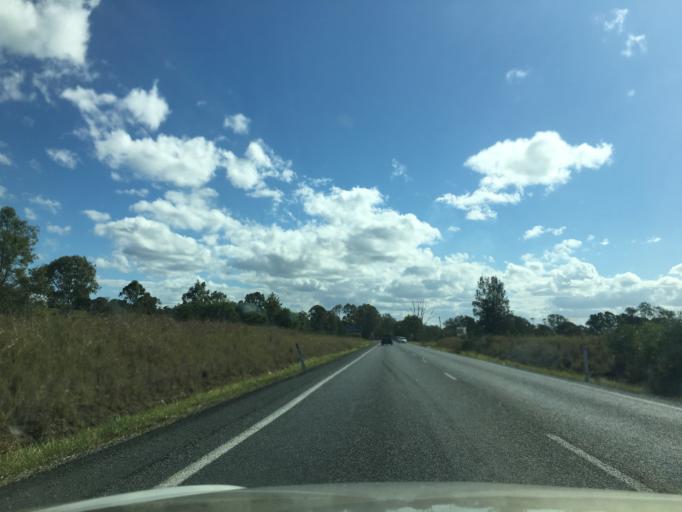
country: AU
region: Queensland
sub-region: Logan
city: Logan Reserve
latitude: -27.7539
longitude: 153.1213
